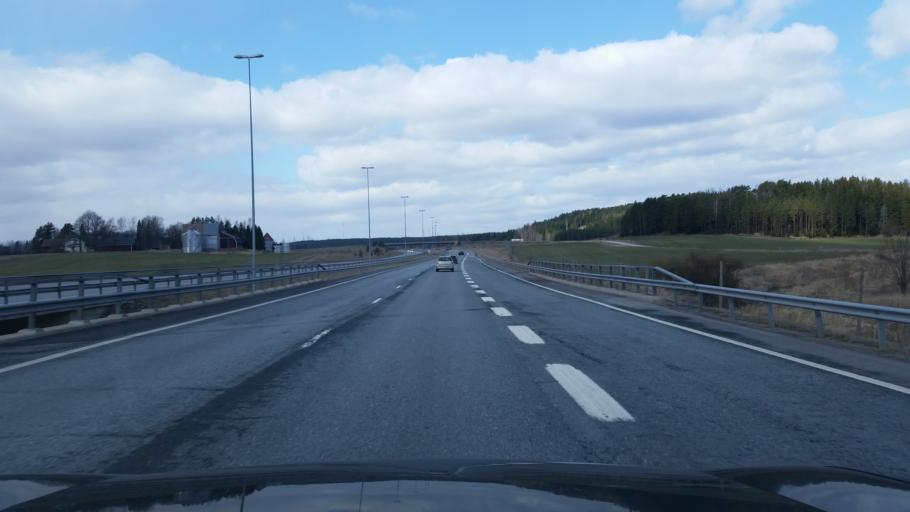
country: FI
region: Varsinais-Suomi
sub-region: Salo
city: Muurla
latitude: 60.3820
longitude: 23.3143
